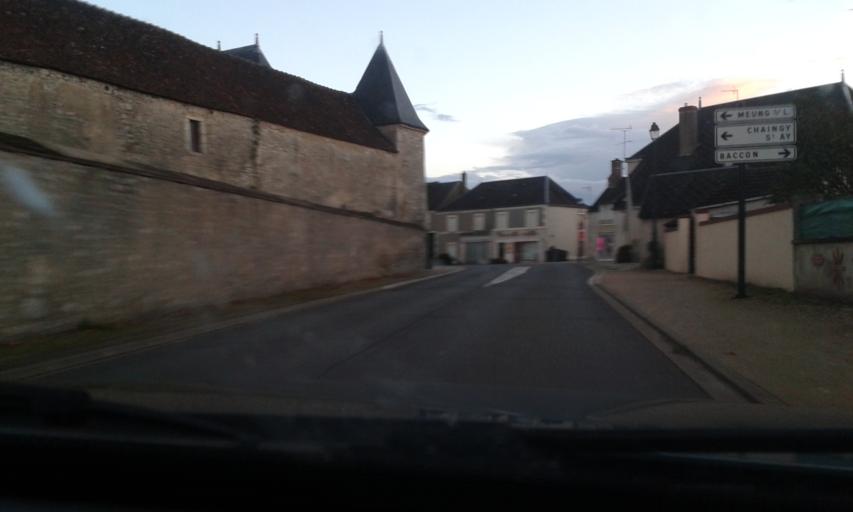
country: FR
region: Centre
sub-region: Departement du Loiret
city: Huisseau-sur-Mauves
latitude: 47.8931
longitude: 1.7039
